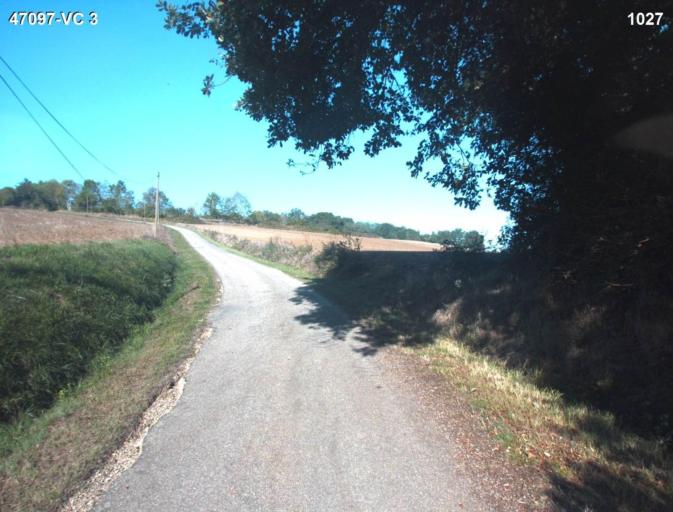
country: FR
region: Aquitaine
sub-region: Departement du Lot-et-Garonne
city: Vianne
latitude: 44.1946
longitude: 0.3562
